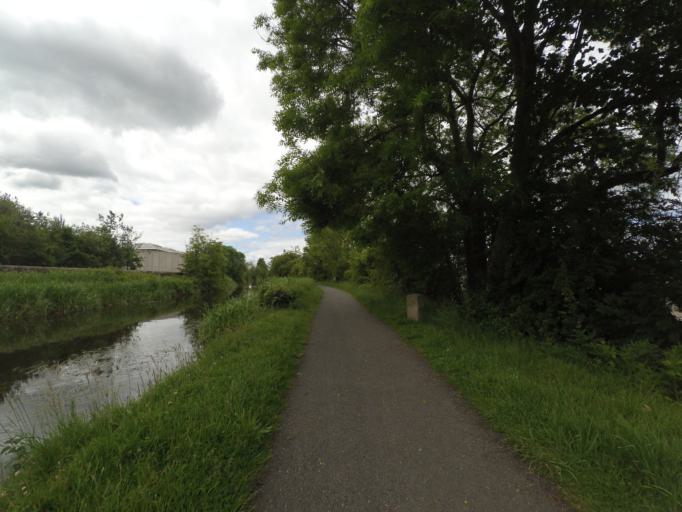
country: GB
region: Scotland
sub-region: Falkirk
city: Polmont
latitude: 55.9845
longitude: -3.7315
